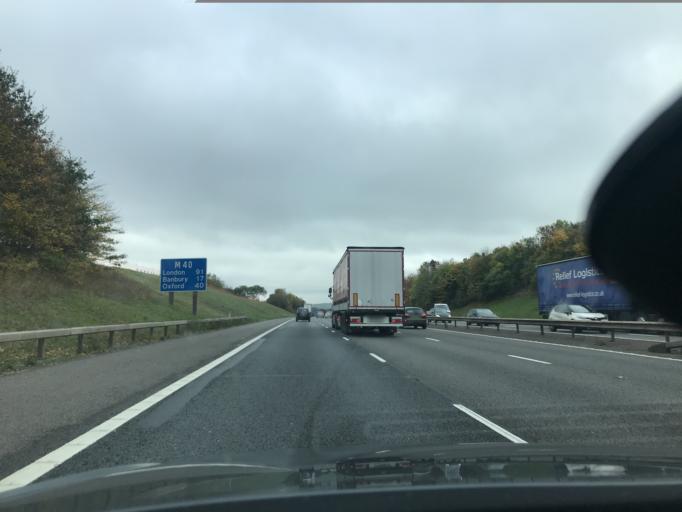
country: GB
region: England
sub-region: Warwickshire
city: Warwick
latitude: 52.2384
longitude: -1.5475
